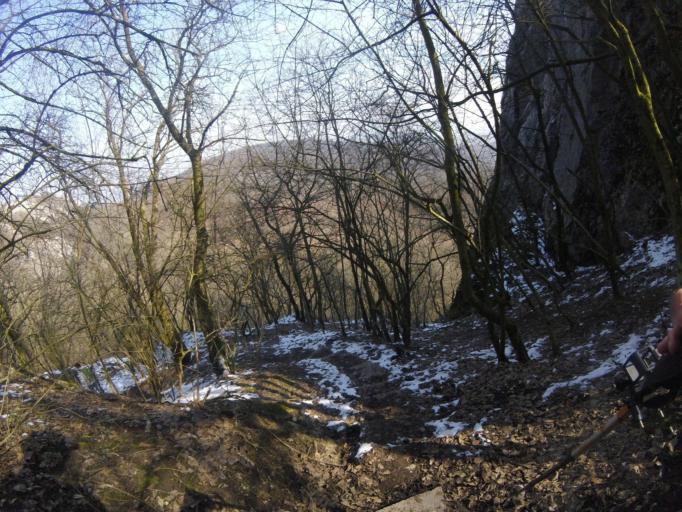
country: HU
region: Komarom-Esztergom
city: Nyergesujfalu
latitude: 47.7325
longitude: 18.5553
